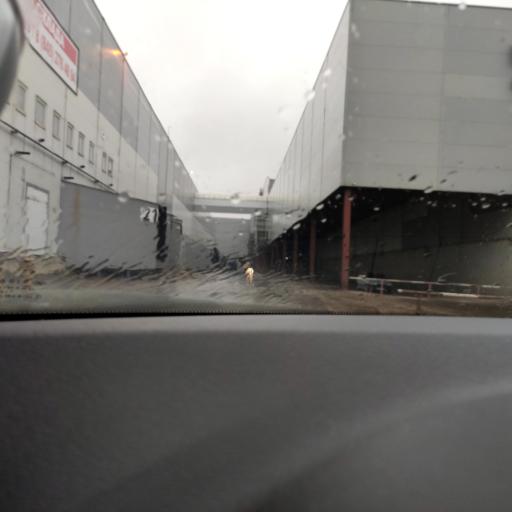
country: RU
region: Samara
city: Petra-Dubrava
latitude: 53.2757
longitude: 50.2745
